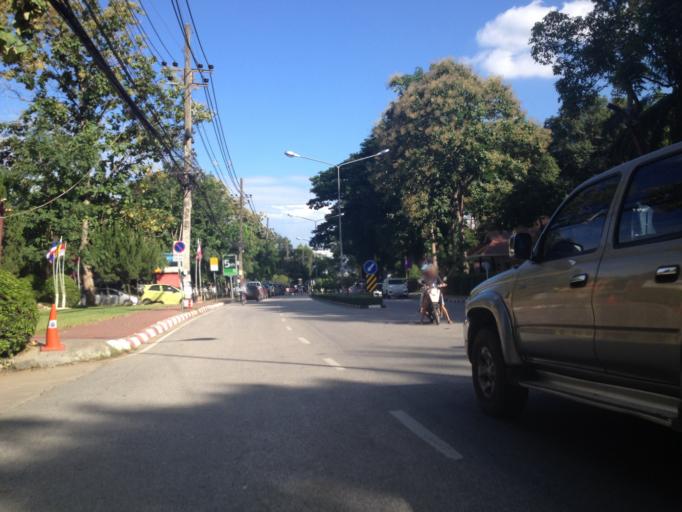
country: TH
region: Chiang Mai
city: Chiang Mai
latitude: 18.8100
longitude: 98.9511
